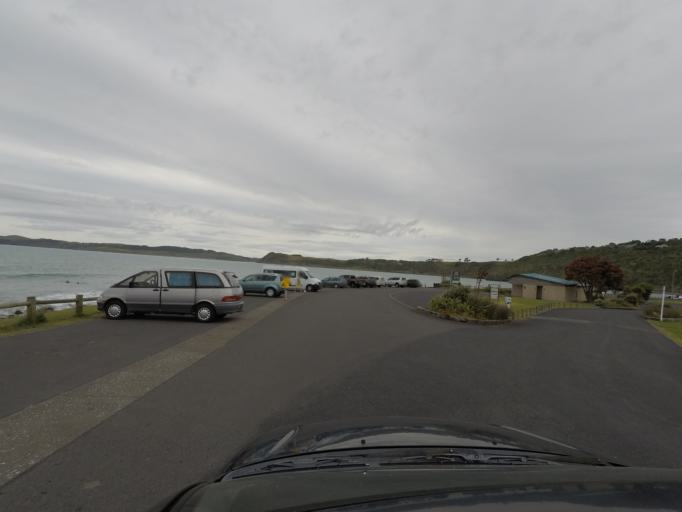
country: NZ
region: Waikato
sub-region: Waikato District
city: Raglan
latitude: -37.8215
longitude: 174.8121
